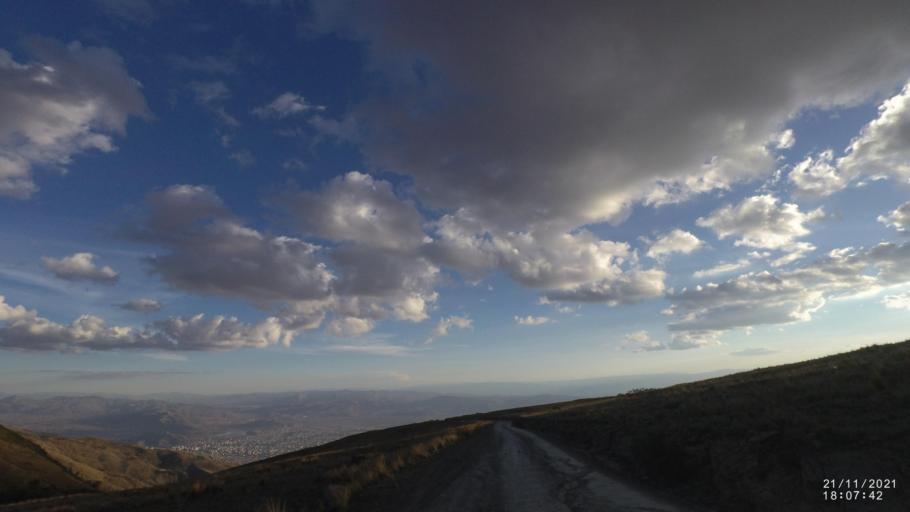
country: BO
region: Cochabamba
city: Cochabamba
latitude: -17.2792
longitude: -66.2101
